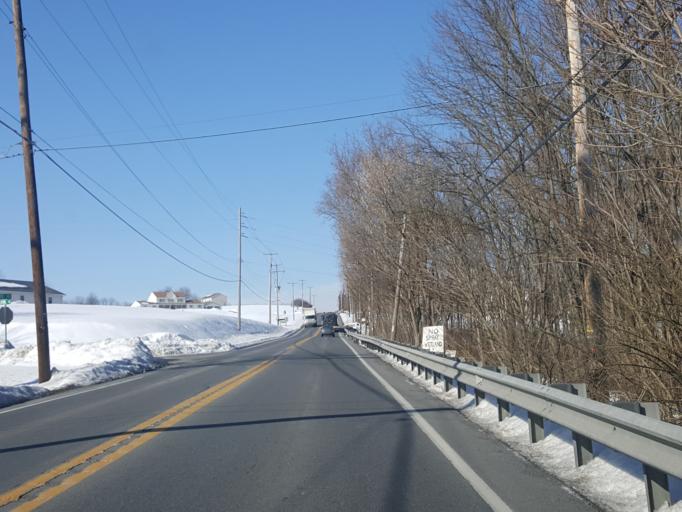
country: US
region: Pennsylvania
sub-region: Berks County
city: Womelsdorf
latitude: 40.4704
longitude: -76.1509
